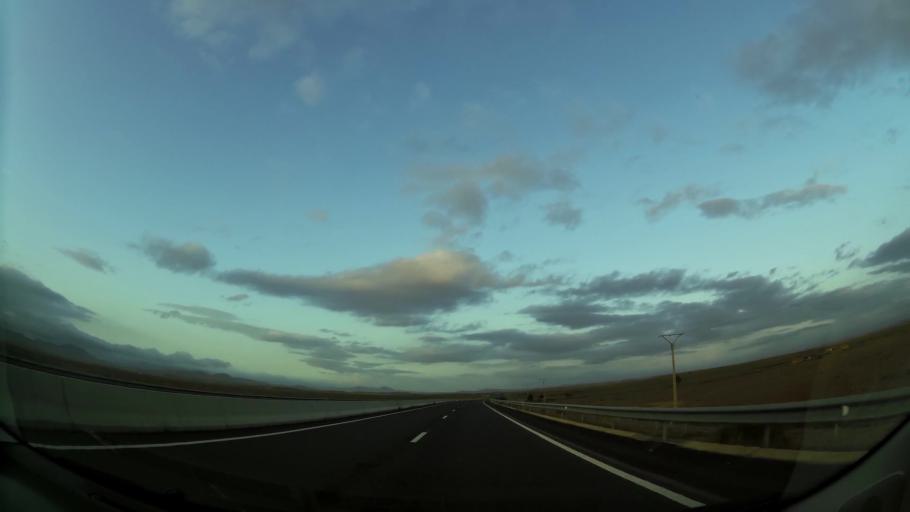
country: MA
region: Oriental
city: Taourirt
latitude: 34.5485
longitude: -2.8929
